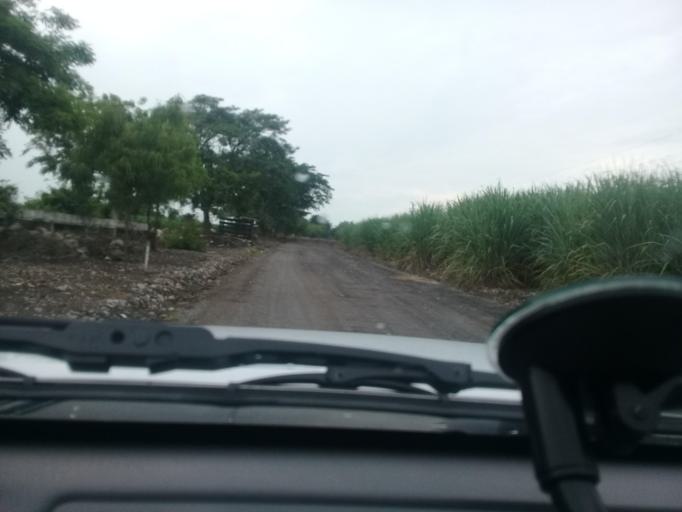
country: MX
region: Veracruz
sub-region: Puente Nacional
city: Cabezas
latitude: 19.3620
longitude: -96.4240
